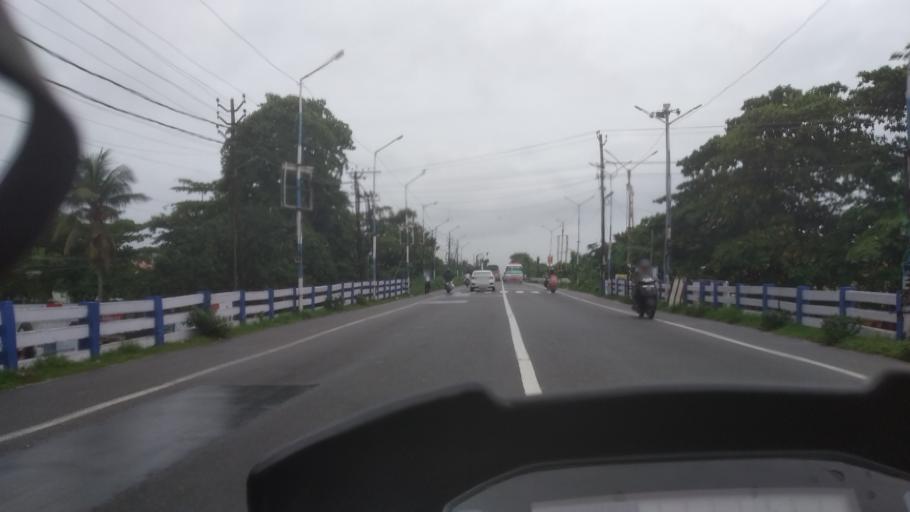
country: IN
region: Kerala
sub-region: Alappuzha
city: Kayankulam
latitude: 9.1716
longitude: 76.4977
